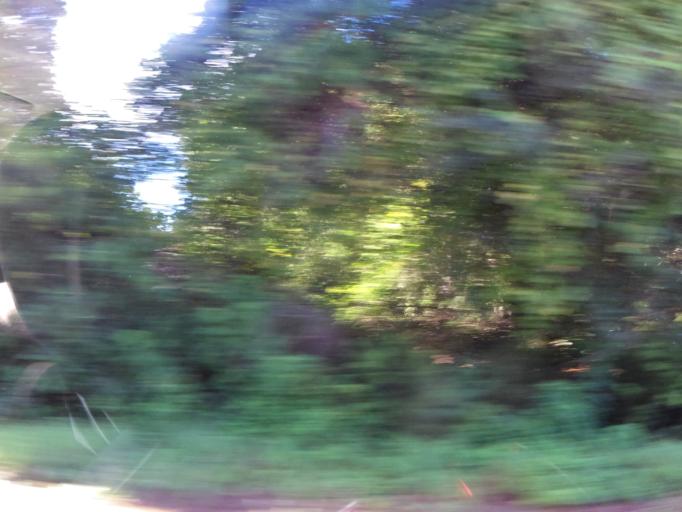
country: US
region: Georgia
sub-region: Glynn County
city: Country Club Estates
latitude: 31.2258
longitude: -81.4758
